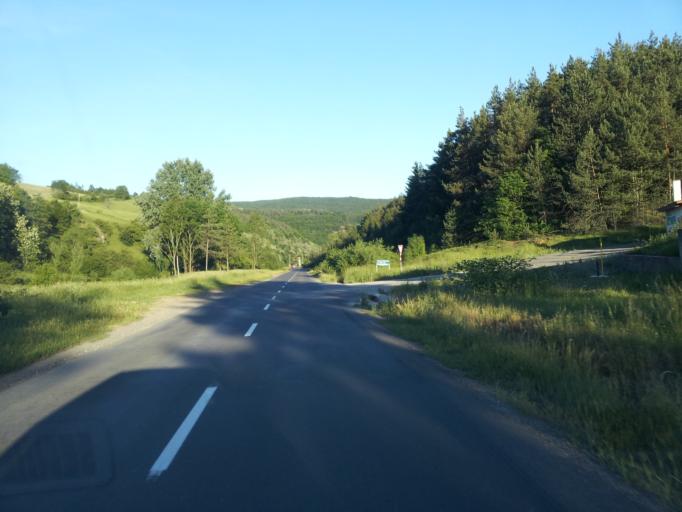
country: SK
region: Banskobystricky
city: Svaety Anton
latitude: 48.4341
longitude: 18.9281
